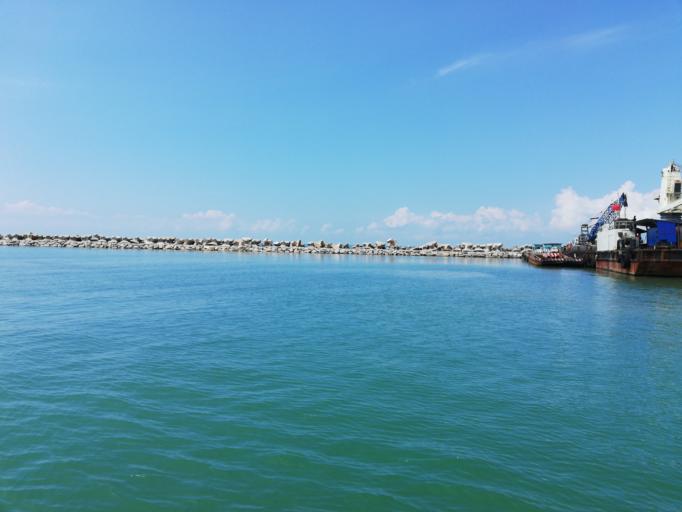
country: LK
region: Western
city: Colombo
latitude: 6.9282
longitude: 79.8230
